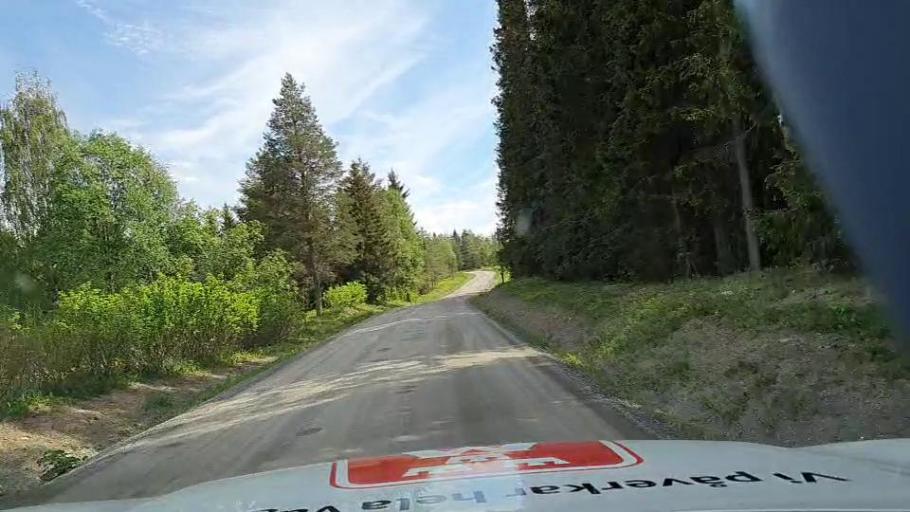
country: SE
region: Jaemtland
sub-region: OEstersunds Kommun
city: Brunflo
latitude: 63.0152
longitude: 14.7761
